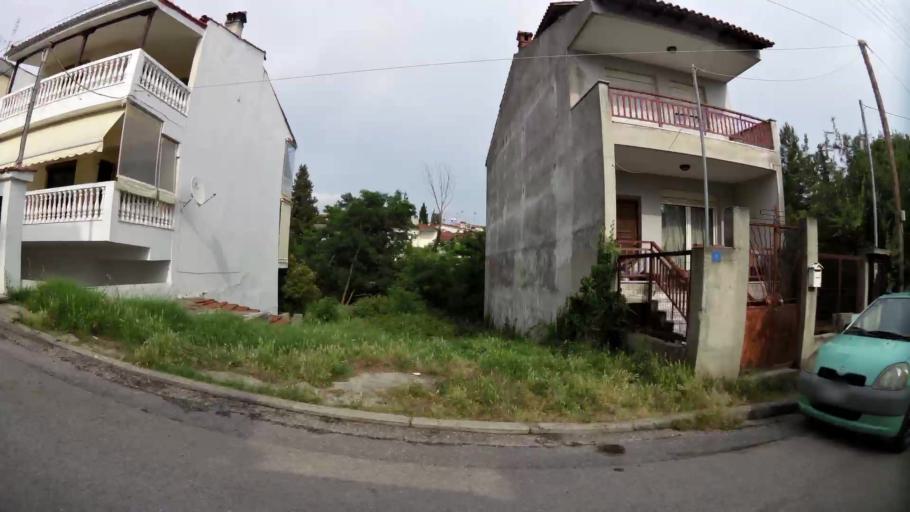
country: GR
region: Central Macedonia
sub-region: Nomos Thessalonikis
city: Oraiokastro
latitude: 40.7315
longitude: 22.9128
